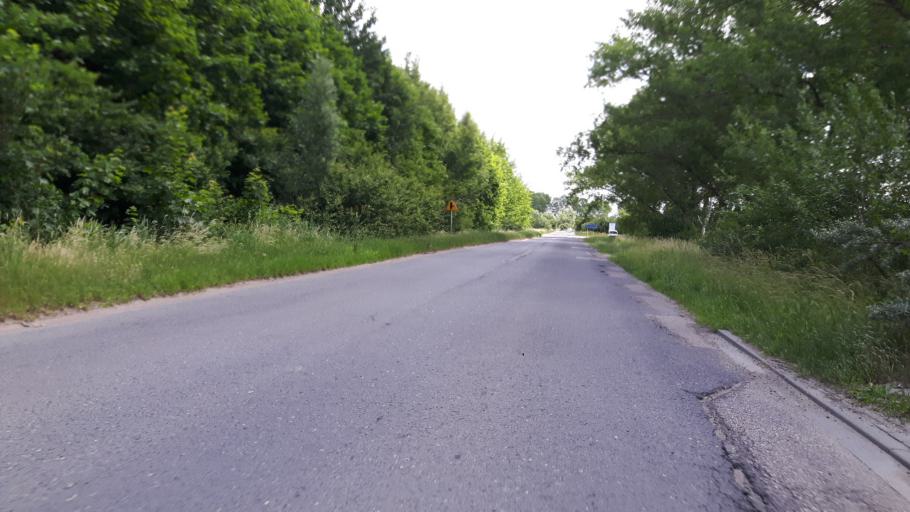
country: PL
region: Pomeranian Voivodeship
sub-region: Gdansk
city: Gdansk
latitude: 54.3391
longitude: 18.7400
